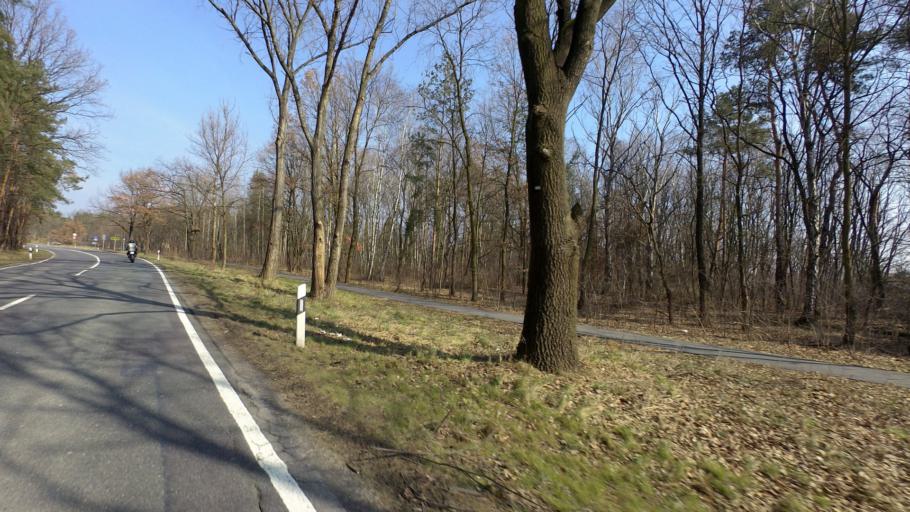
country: DE
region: Brandenburg
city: Werder
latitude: 52.4065
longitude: 12.9066
